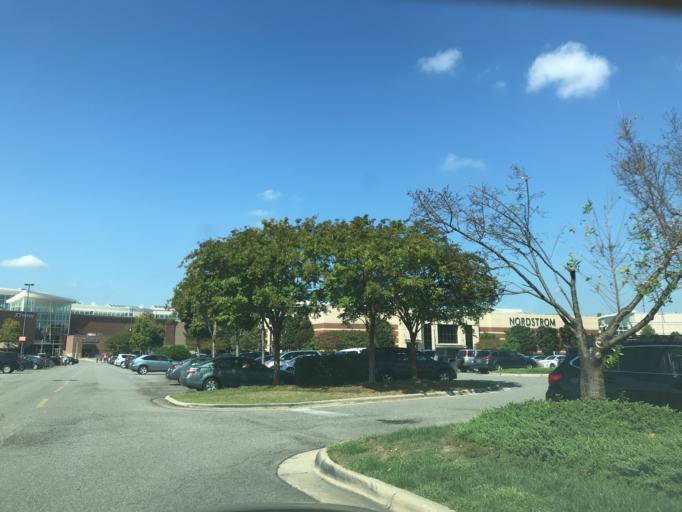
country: US
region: North Carolina
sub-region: Durham County
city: Durham
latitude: 35.9027
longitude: -78.9397
